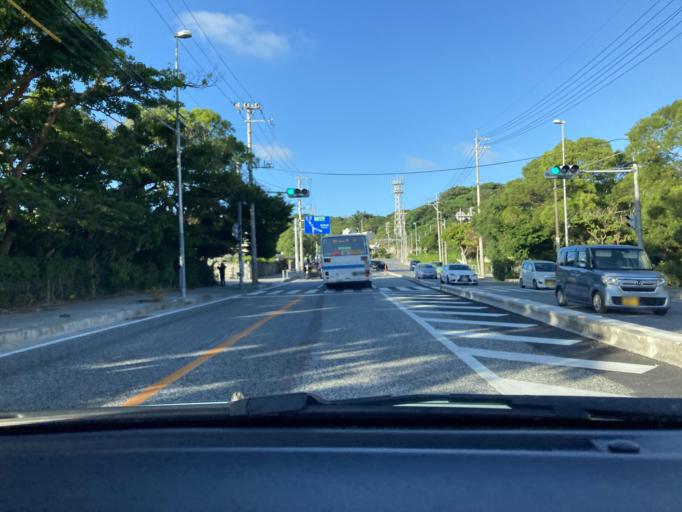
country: JP
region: Okinawa
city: Naha-shi
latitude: 26.2062
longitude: 127.7226
